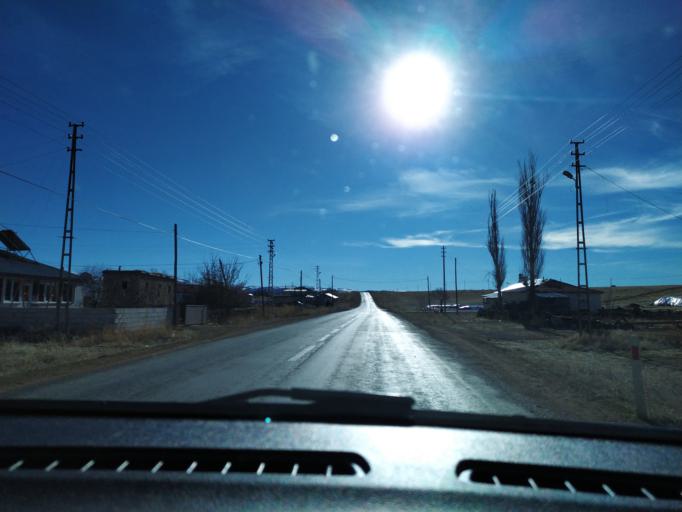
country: TR
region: Kayseri
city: Orensehir
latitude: 38.9076
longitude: 36.7322
